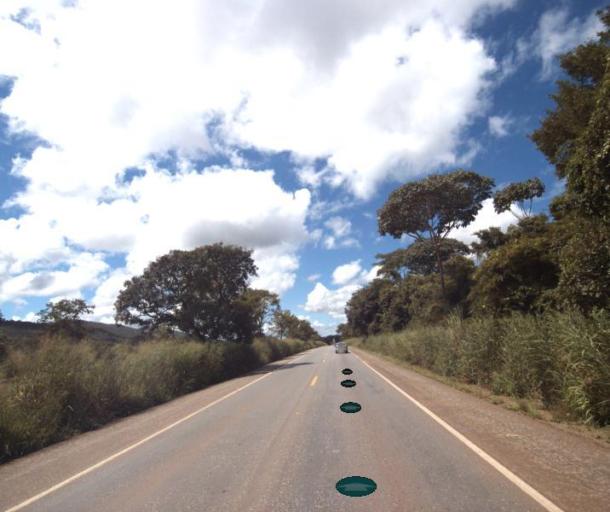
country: BR
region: Goias
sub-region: Petrolina De Goias
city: Petrolina de Goias
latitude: -15.9637
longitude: -49.1771
